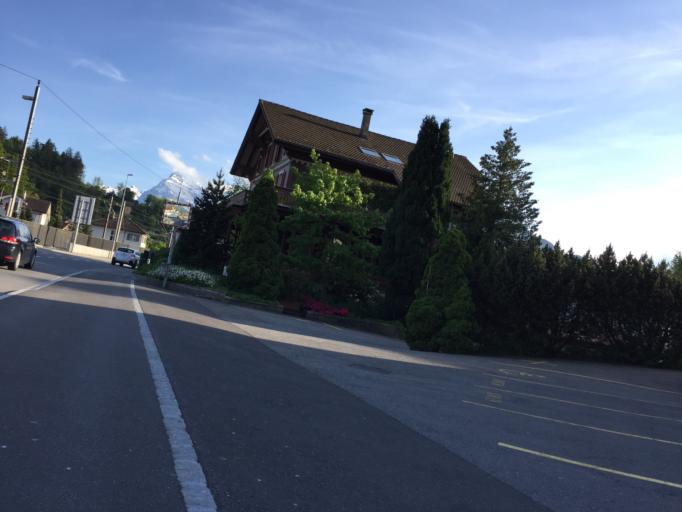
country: CH
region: Schwyz
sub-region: Bezirk Schwyz
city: Ingenbohl
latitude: 46.9987
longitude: 8.6094
